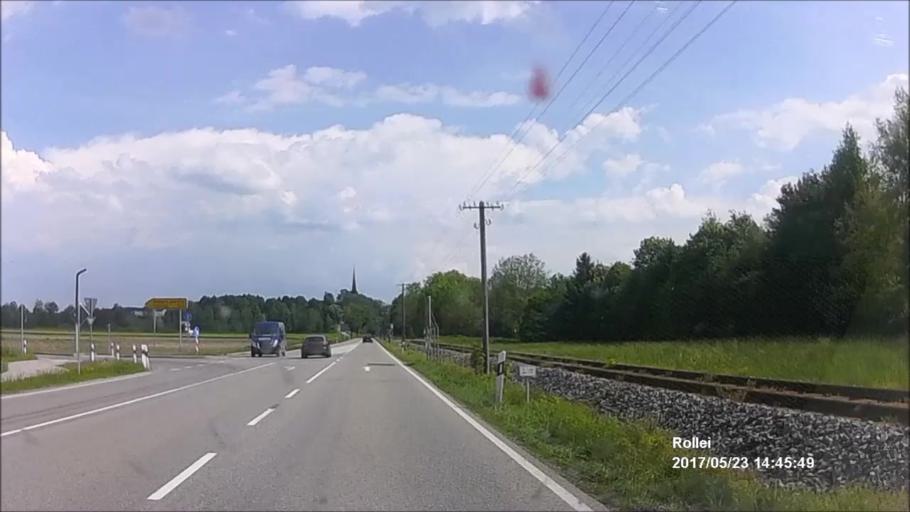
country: DE
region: Bavaria
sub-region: Upper Bavaria
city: Traunreut
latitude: 47.9782
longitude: 12.5571
